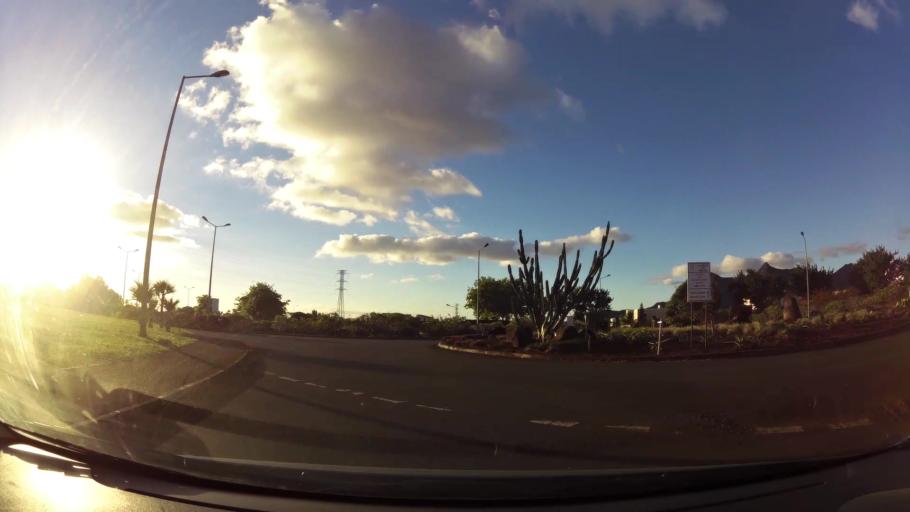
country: MU
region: Plaines Wilhems
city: Ebene
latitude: -20.2374
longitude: 57.4807
